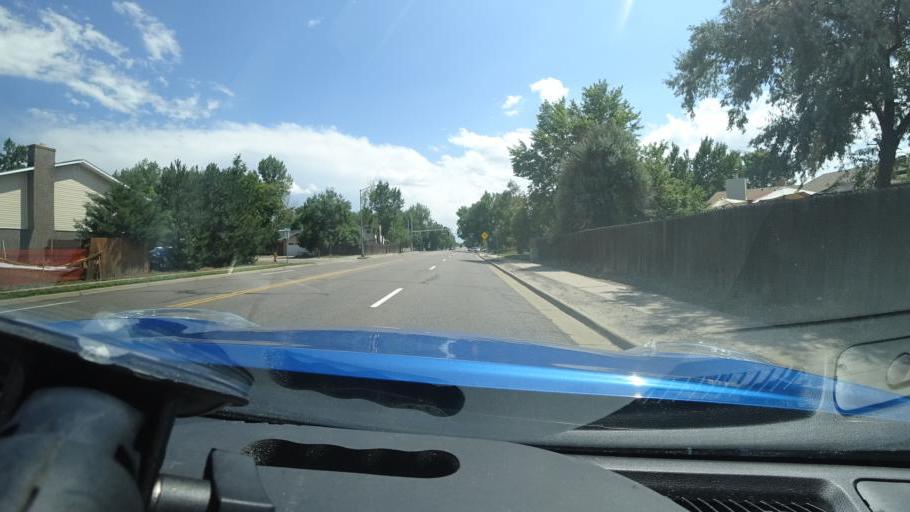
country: US
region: Colorado
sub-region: Adams County
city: Aurora
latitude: 39.6905
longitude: -104.8472
